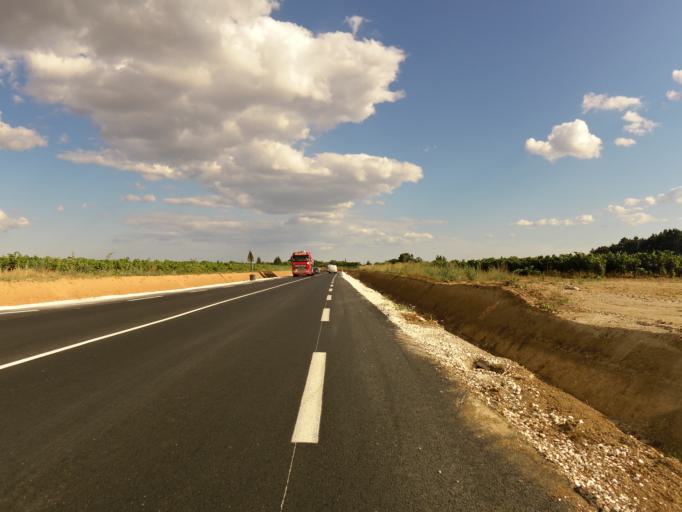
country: FR
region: Languedoc-Roussillon
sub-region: Departement du Gard
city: Mus
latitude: 43.7256
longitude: 4.1936
